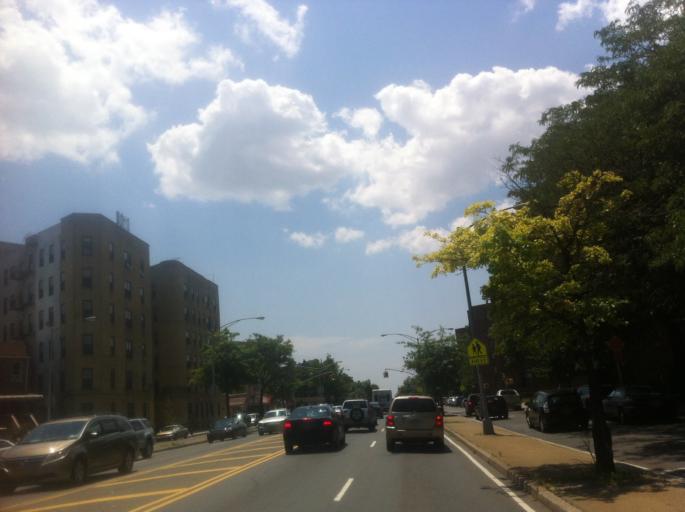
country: US
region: New York
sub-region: Kings County
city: Brooklyn
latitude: 40.6602
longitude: -73.9200
